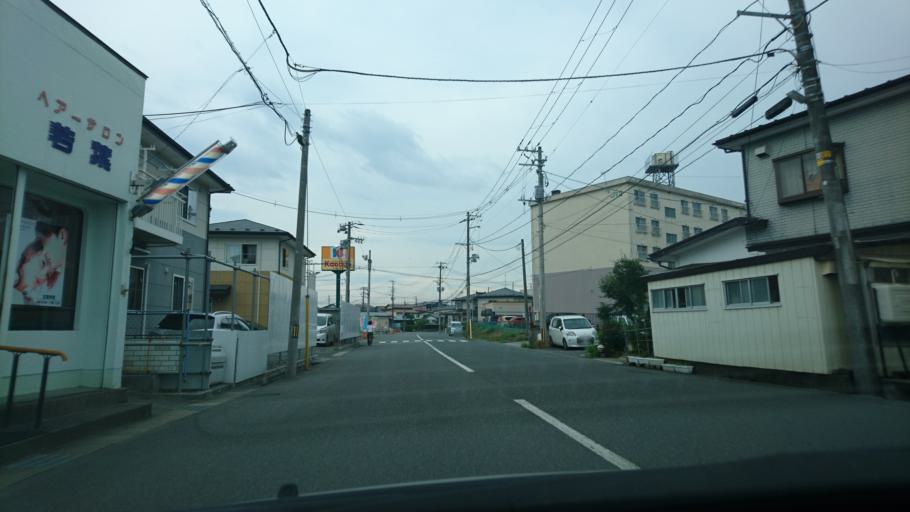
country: JP
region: Iwate
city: Ichinoseki
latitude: 38.9324
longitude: 141.1435
